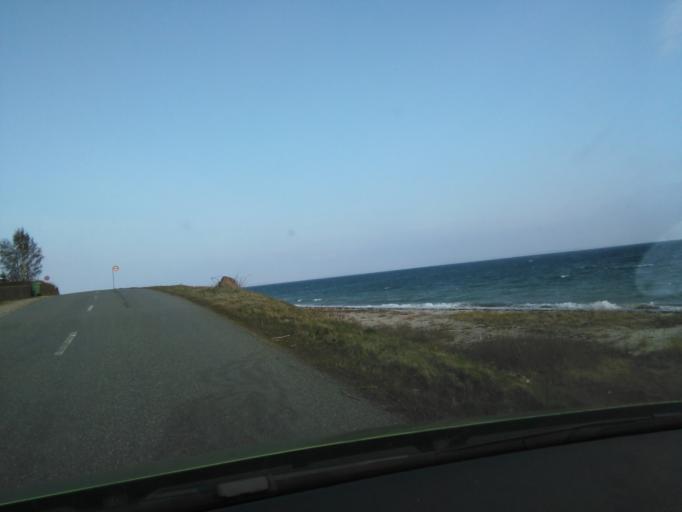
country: DK
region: Central Jutland
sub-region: Arhus Kommune
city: Beder
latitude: 56.0314
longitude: 10.2681
